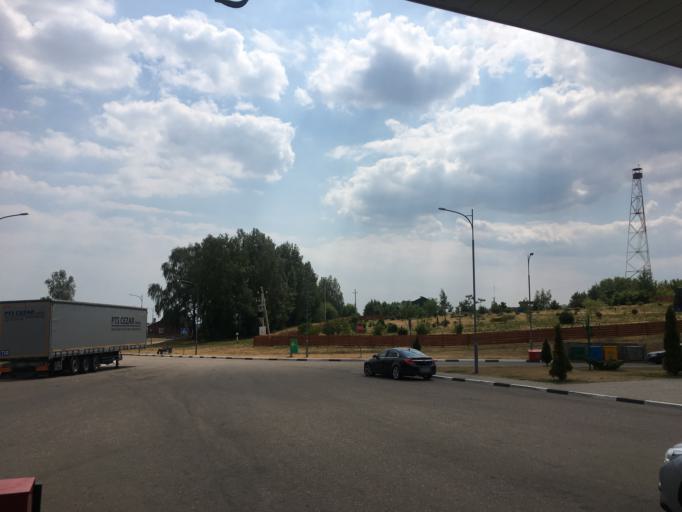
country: BY
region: Brest
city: Ruzhany
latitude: 52.8712
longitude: 24.8737
